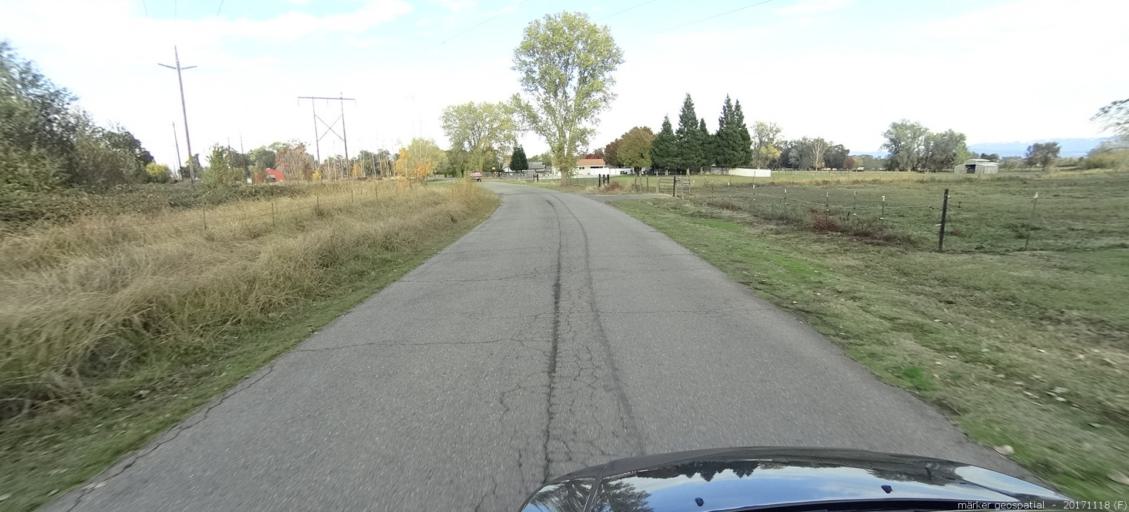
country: US
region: California
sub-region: Shasta County
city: Anderson
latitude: 40.4561
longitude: -122.3293
